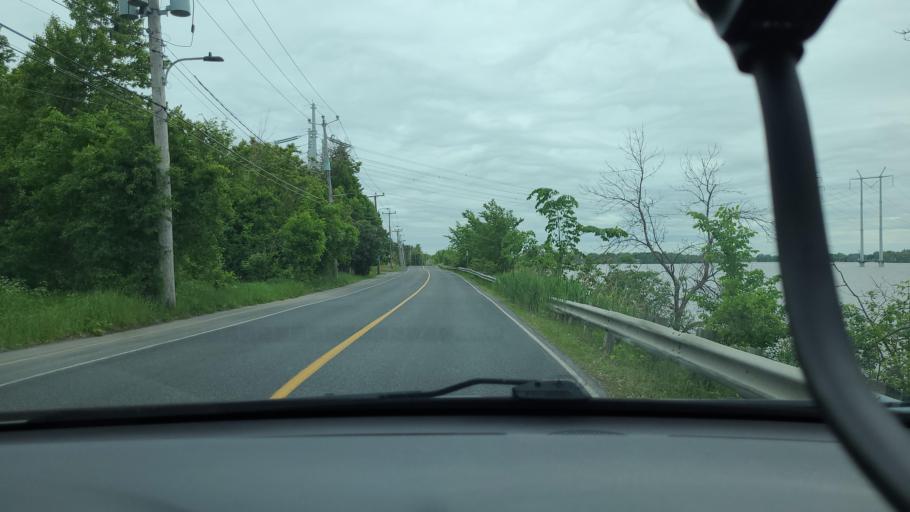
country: CA
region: Quebec
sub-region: Lanaudiere
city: Charlemagne
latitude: 45.6986
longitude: -73.5103
